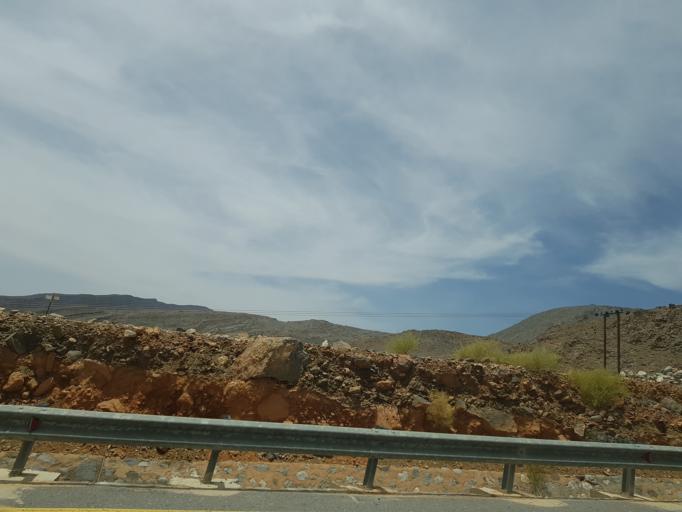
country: OM
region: Muhafazat ad Dakhiliyah
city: Izki
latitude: 22.9763
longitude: 57.6990
